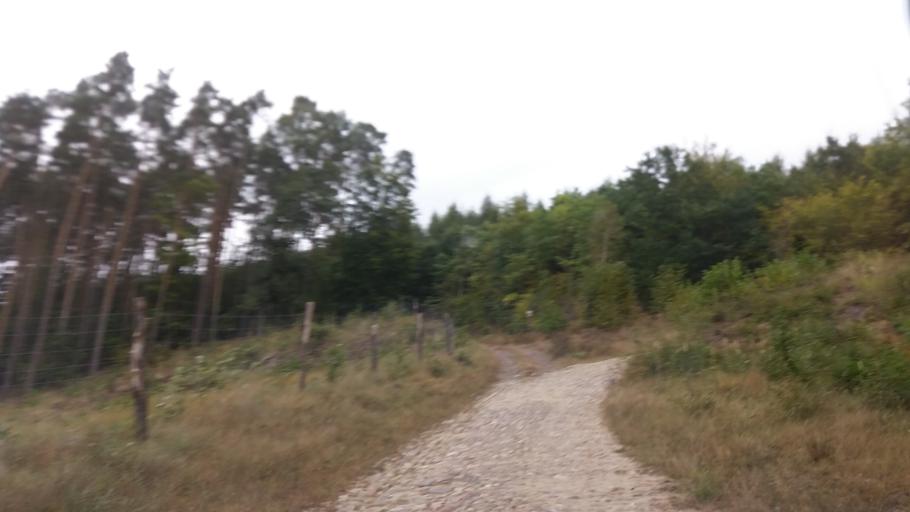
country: PL
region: West Pomeranian Voivodeship
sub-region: Powiat choszczenski
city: Bierzwnik
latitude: 52.9767
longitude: 15.6153
